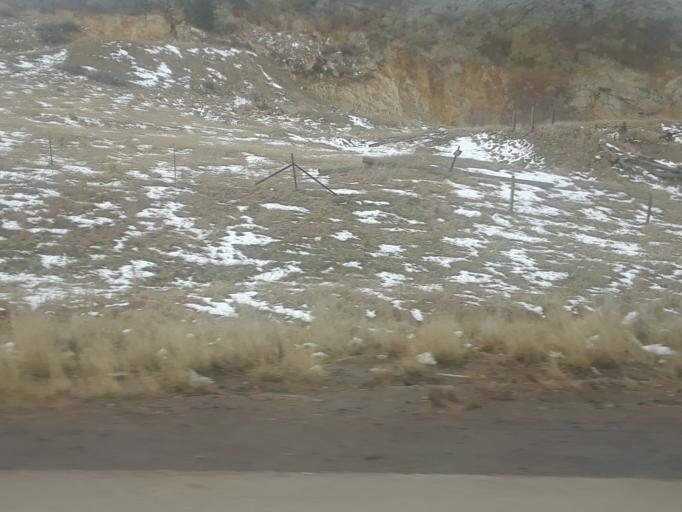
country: US
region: Colorado
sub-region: Jefferson County
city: Golden
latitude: 39.8512
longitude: -105.2331
